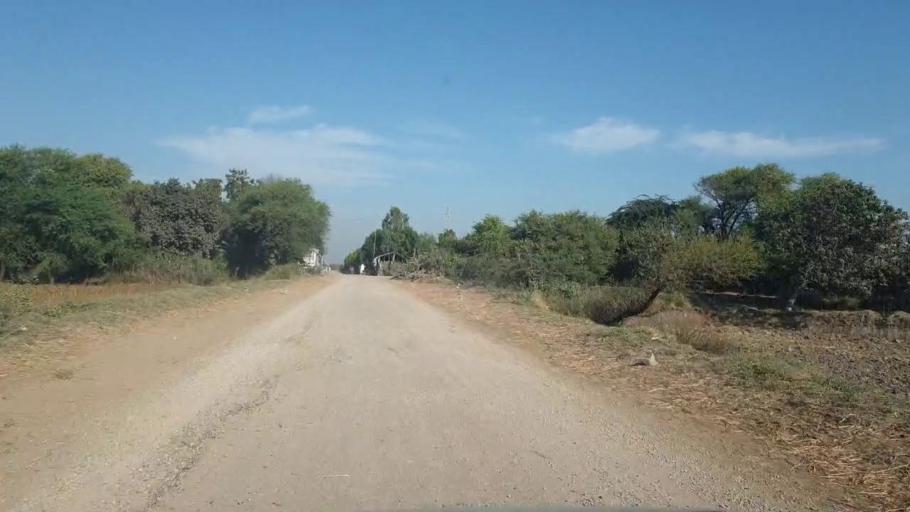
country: PK
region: Sindh
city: Talhar
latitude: 24.9445
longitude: 68.7873
